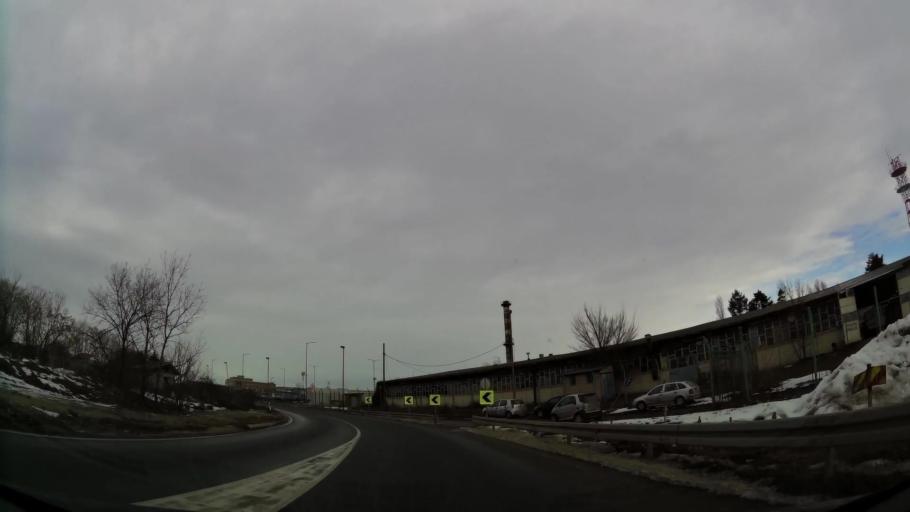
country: RS
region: Central Serbia
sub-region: Belgrade
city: Surcin
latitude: 44.8131
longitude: 20.2924
